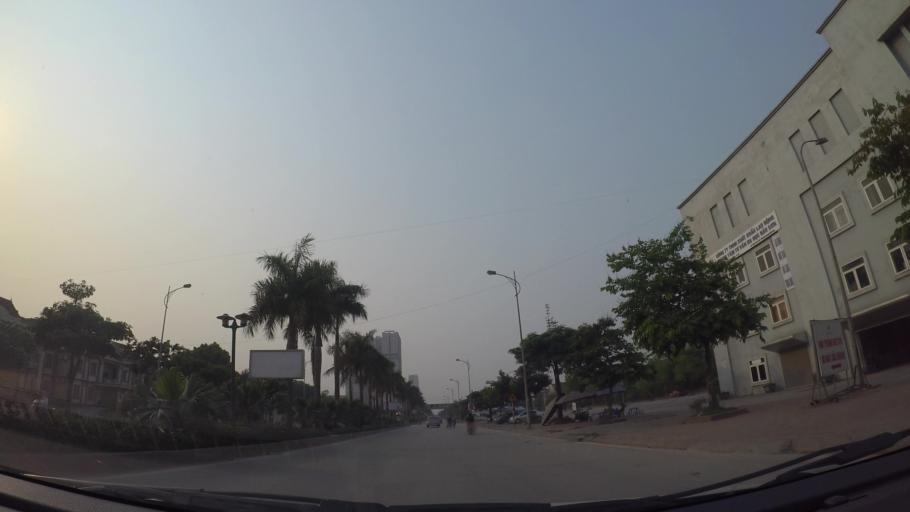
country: VN
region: Ha Noi
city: Ha Dong
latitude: 20.9981
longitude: 105.7344
